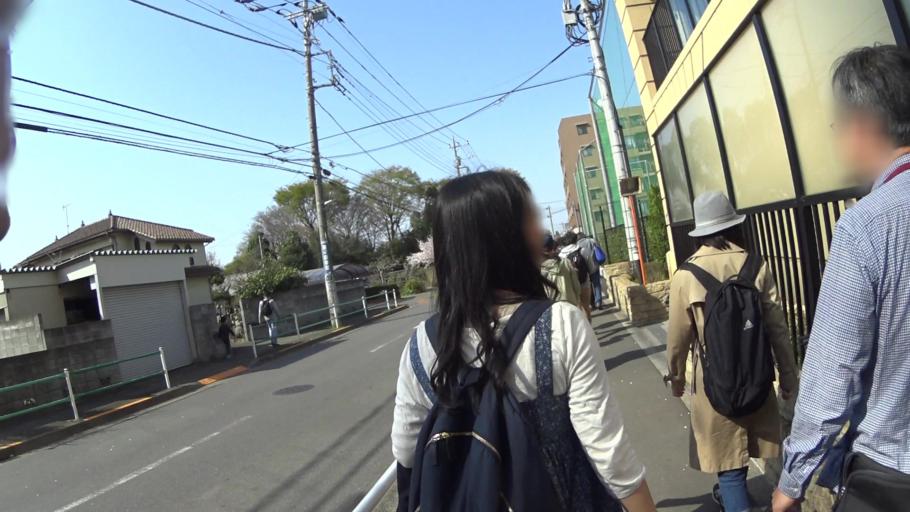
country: JP
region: Tokyo
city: Kokubunji
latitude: 35.7148
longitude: 139.4913
